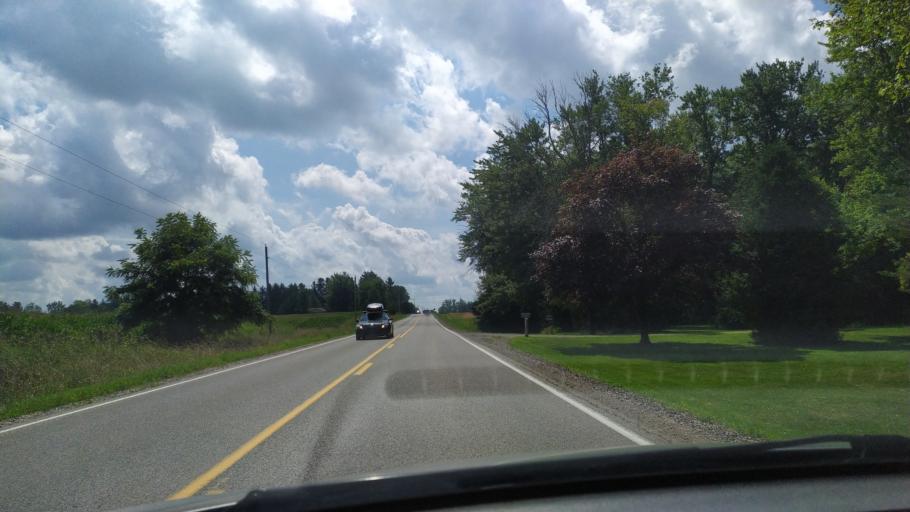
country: CA
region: Ontario
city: London
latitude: 43.0469
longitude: -81.3253
